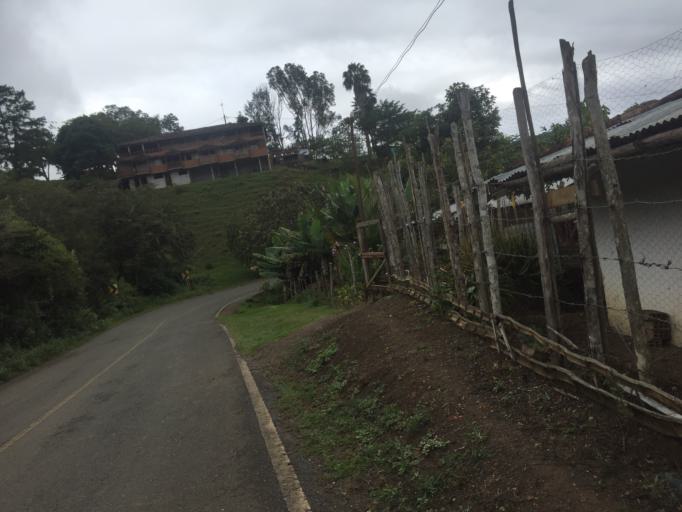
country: CO
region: Valle del Cauca
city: Dagua
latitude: 3.6930
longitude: -76.5908
